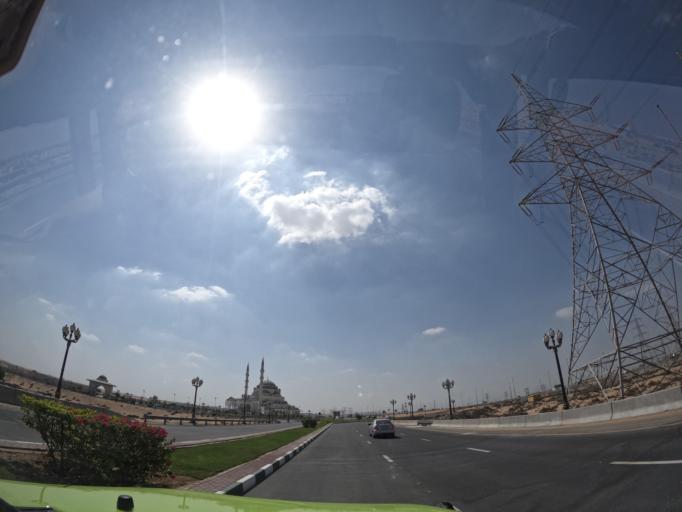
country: AE
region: Ash Shariqah
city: Sharjah
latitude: 25.2447
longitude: 55.5710
